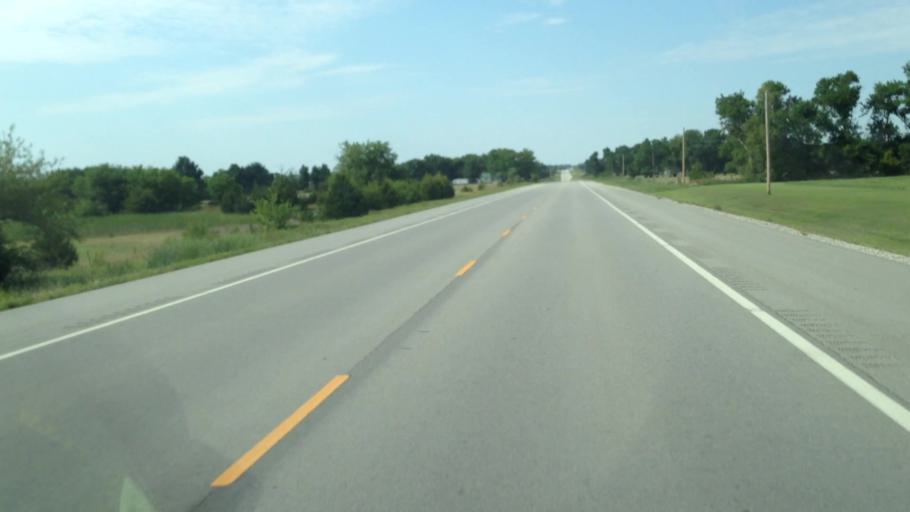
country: US
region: Kansas
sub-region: Labette County
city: Altamont
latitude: 37.2616
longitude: -95.2672
